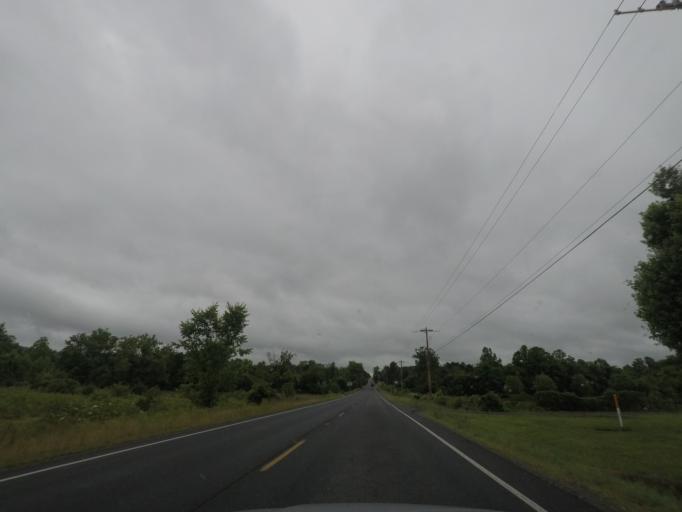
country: US
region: Virginia
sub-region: Prince William County
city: Bull Run Mountain Estates
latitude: 38.8868
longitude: -77.6327
